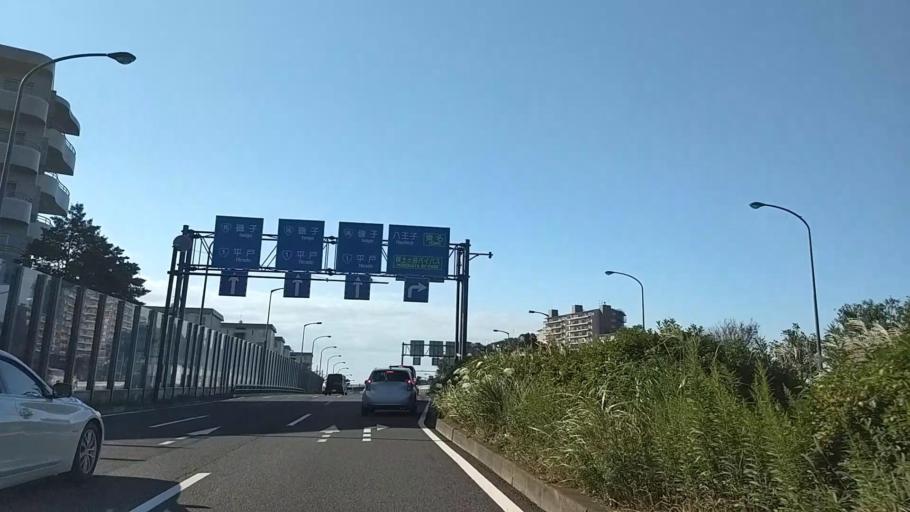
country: JP
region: Kanagawa
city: Yokohama
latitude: 35.4534
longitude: 139.5623
